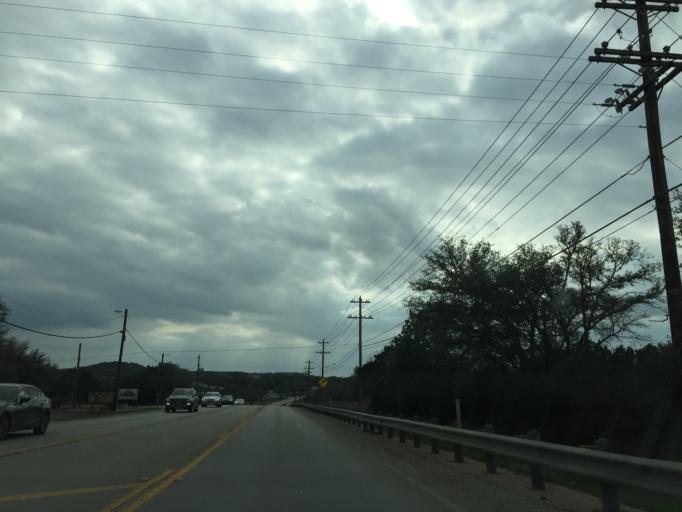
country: US
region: Texas
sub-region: Travis County
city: Shady Hollow
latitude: 30.1614
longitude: -97.9534
